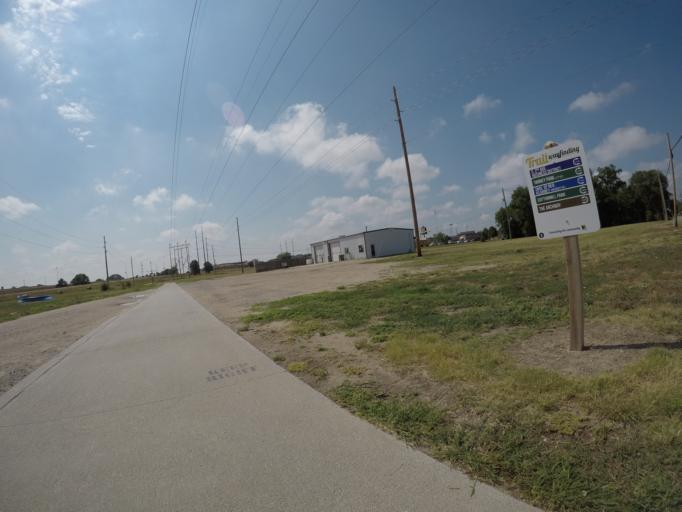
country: US
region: Nebraska
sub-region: Buffalo County
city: Kearney
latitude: 40.6711
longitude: -99.0825
